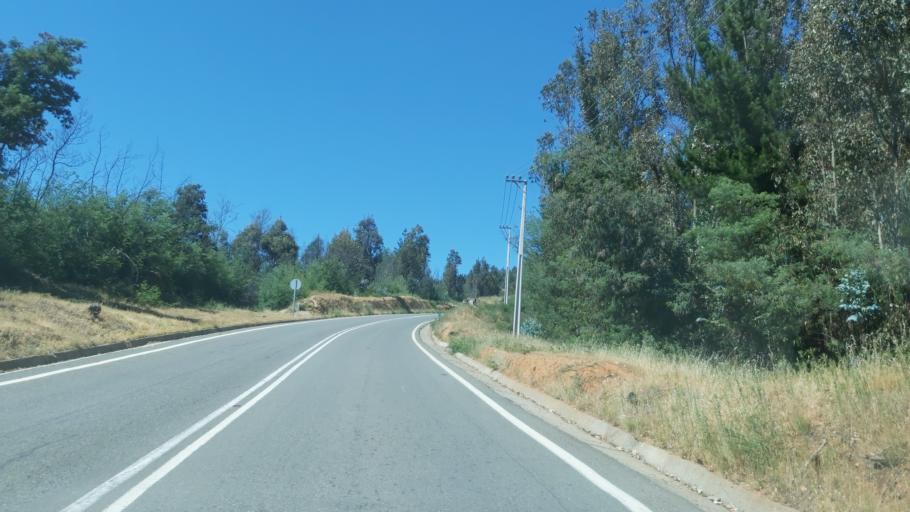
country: CL
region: Maule
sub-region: Provincia de Talca
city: Constitucion
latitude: -34.9048
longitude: -71.9946
